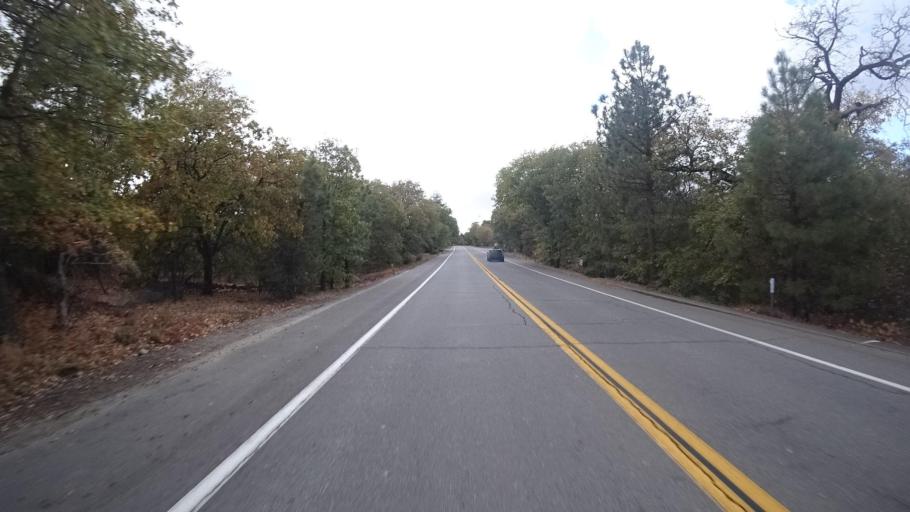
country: US
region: California
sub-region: San Diego County
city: Pine Valley
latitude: 32.8482
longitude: -116.4284
